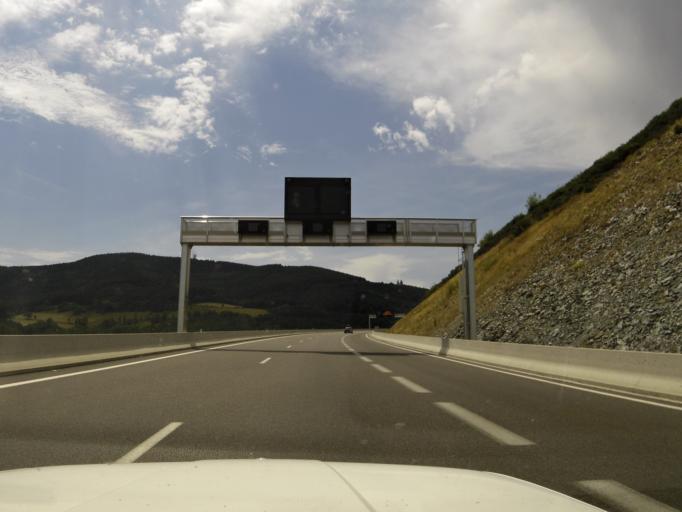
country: FR
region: Rhone-Alpes
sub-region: Departement de la Loire
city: Violay
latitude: 45.8681
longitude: 4.3956
